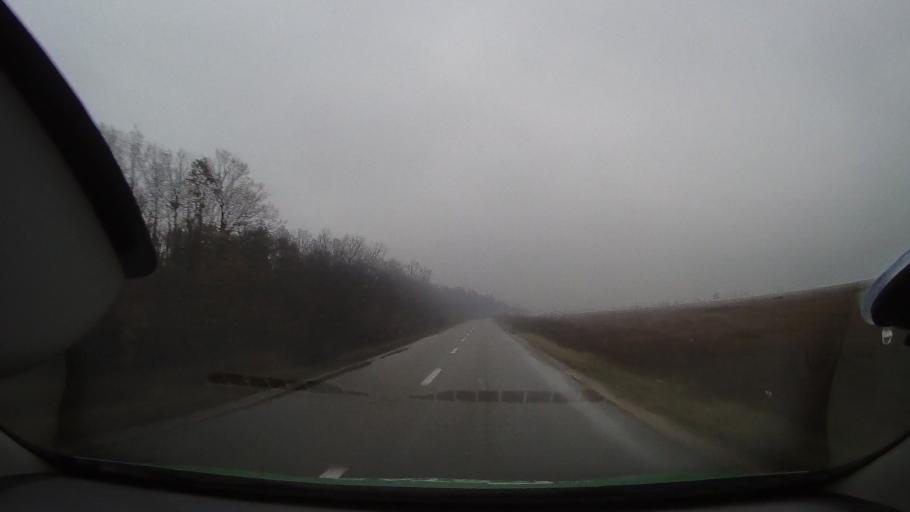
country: RO
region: Bihor
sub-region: Comuna Tinca
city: Gurbediu
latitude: 46.7807
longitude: 21.8715
